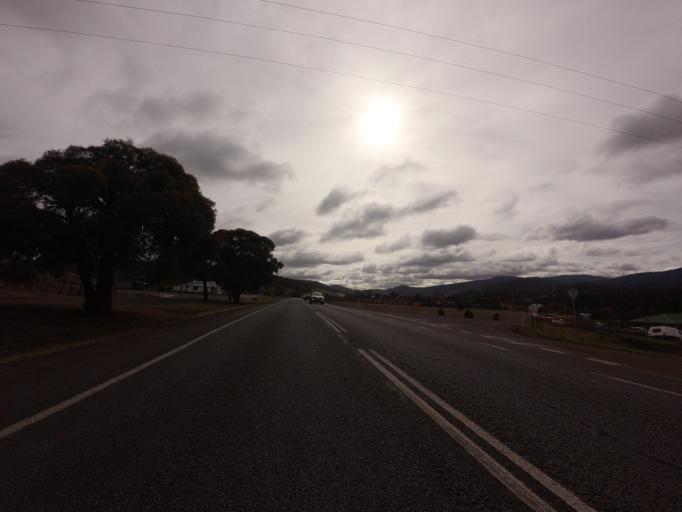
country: AU
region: Tasmania
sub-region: Brighton
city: Bridgewater
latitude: -42.6330
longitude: 147.2244
